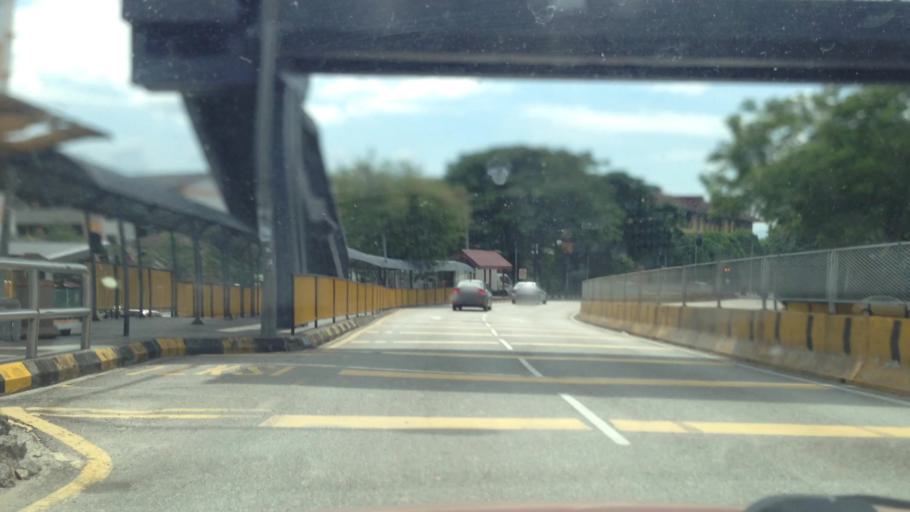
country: MY
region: Kuala Lumpur
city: Kuala Lumpur
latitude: 3.0920
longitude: 101.6825
